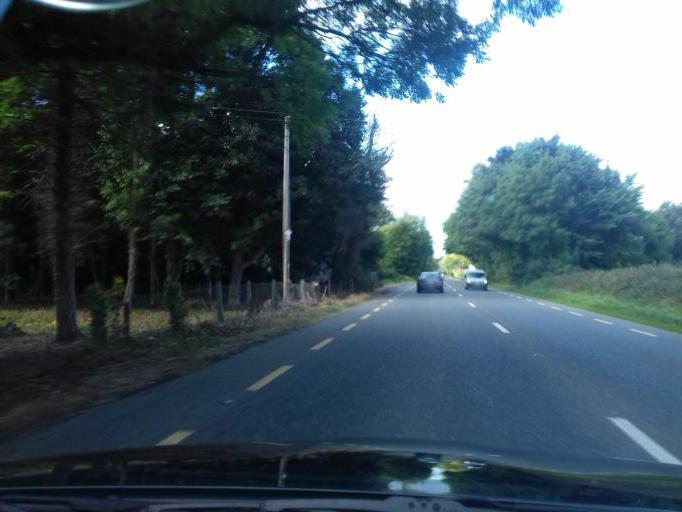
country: IE
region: Leinster
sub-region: An Iarmhi
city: Kilbeggan
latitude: 53.3200
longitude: -7.5112
